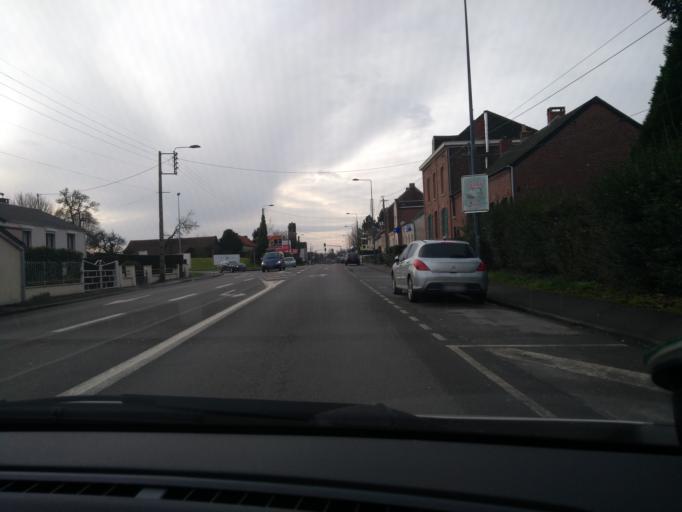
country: FR
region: Nord-Pas-de-Calais
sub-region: Departement du Nord
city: Maubeuge
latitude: 50.2935
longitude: 3.9758
